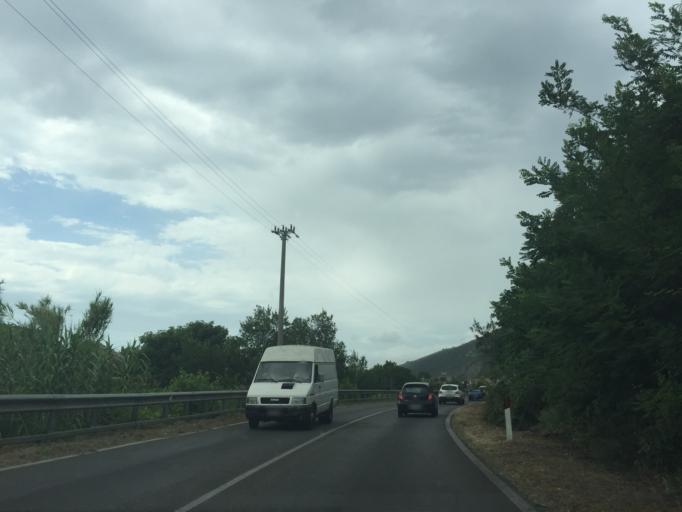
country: IT
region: Tuscany
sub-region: Province of Pisa
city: San Giuliano Terme
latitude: 43.7539
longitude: 10.4443
